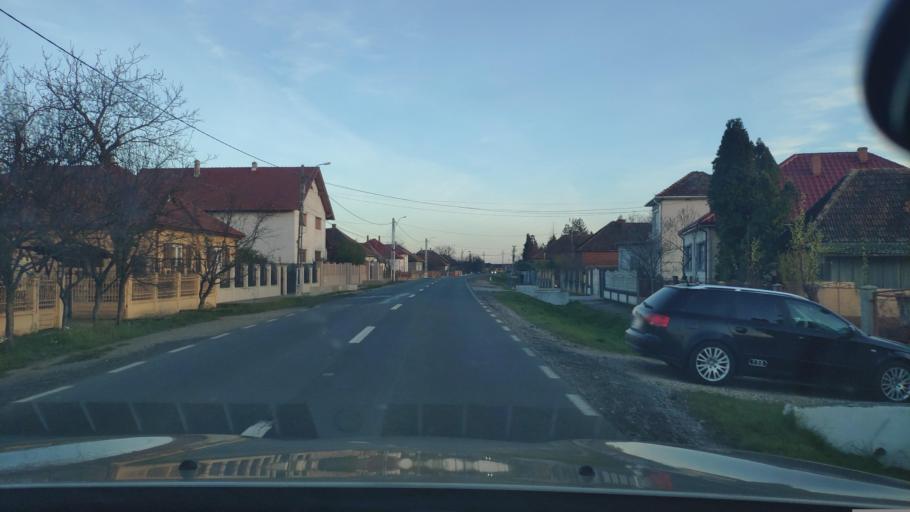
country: RO
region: Satu Mare
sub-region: Comuna Apa
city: Apa
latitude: 47.7652
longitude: 23.1853
